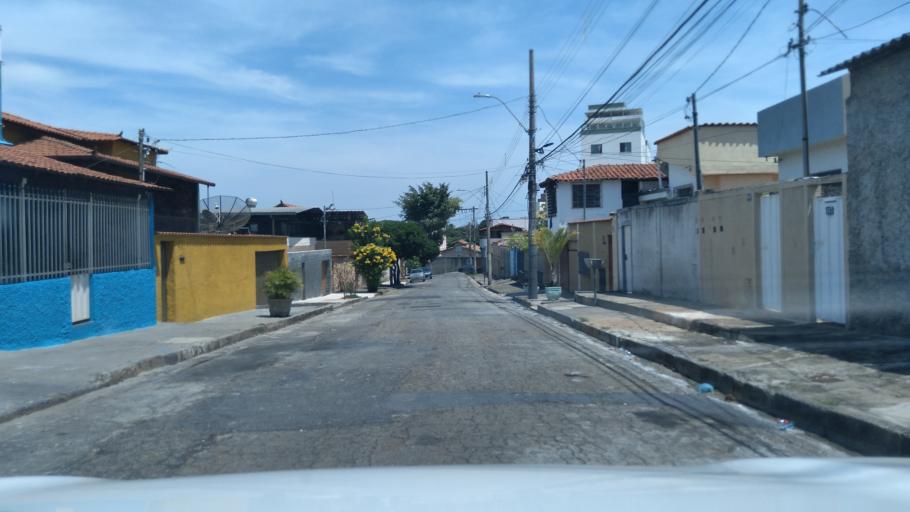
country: BR
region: Minas Gerais
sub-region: Contagem
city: Contagem
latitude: -19.9049
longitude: -44.0156
